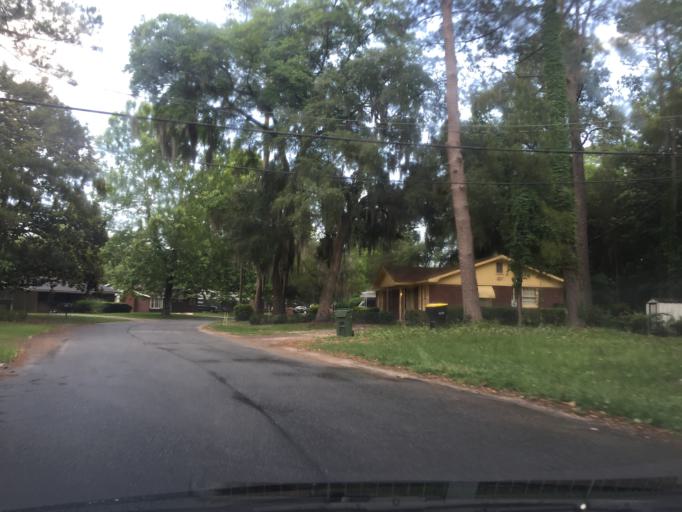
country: US
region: Georgia
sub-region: Chatham County
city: Montgomery
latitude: 31.9925
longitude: -81.1196
